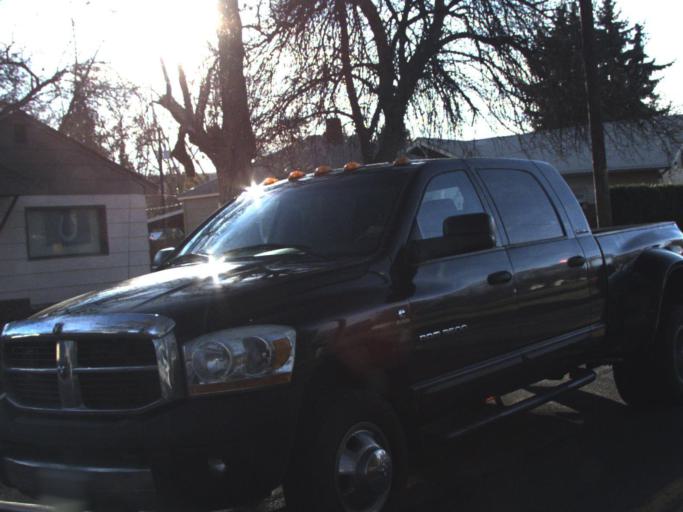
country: US
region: Washington
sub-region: Walla Walla County
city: Waitsburg
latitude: 46.2701
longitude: -118.1519
